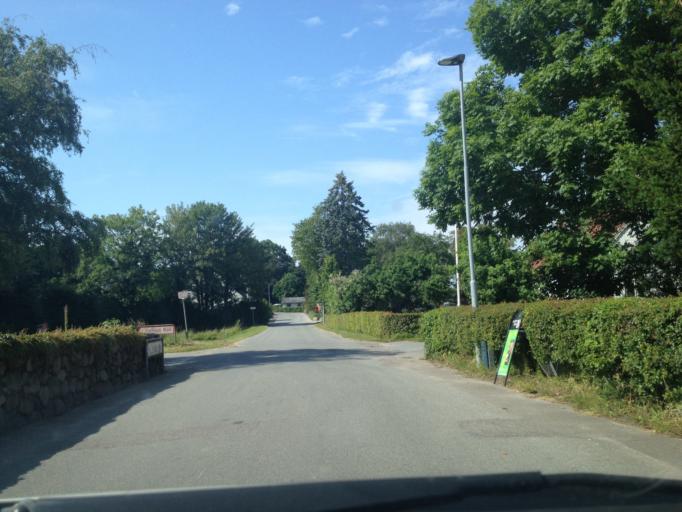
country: DK
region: Central Jutland
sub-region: Samso Kommune
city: Tranebjerg
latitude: 55.8115
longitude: 10.5561
